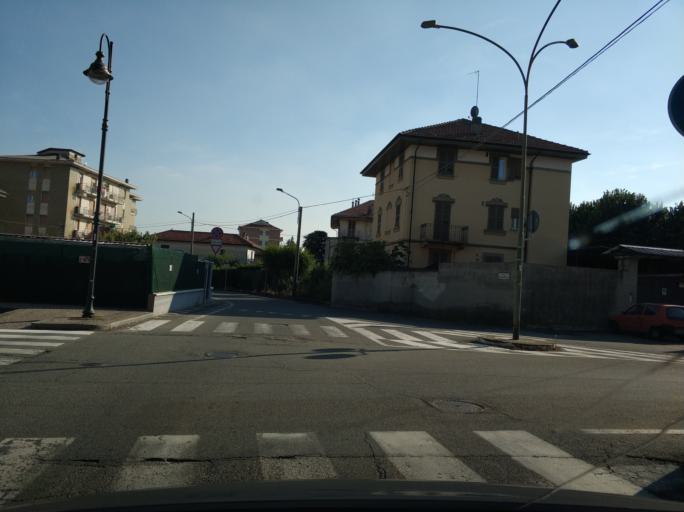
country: IT
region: Piedmont
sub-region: Provincia di Torino
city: San Maurizio
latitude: 45.2169
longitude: 7.6324
